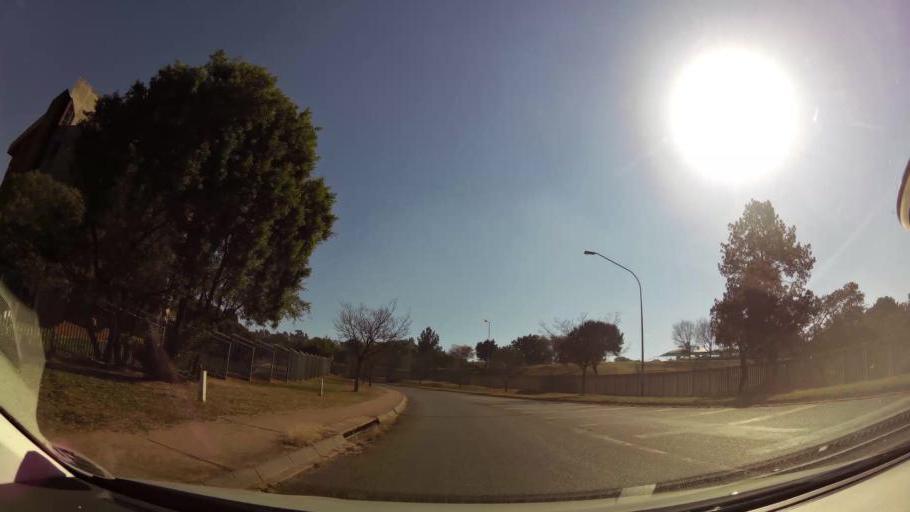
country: ZA
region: Gauteng
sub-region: City of Tshwane Metropolitan Municipality
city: Pretoria
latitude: -25.7688
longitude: 28.2097
